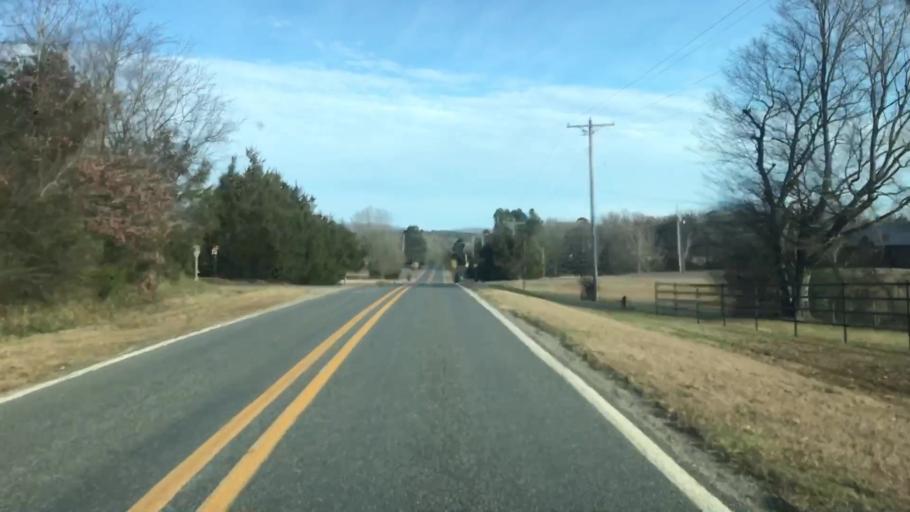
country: US
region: Arkansas
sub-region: Garland County
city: Rockwell
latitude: 34.5046
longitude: -93.2762
